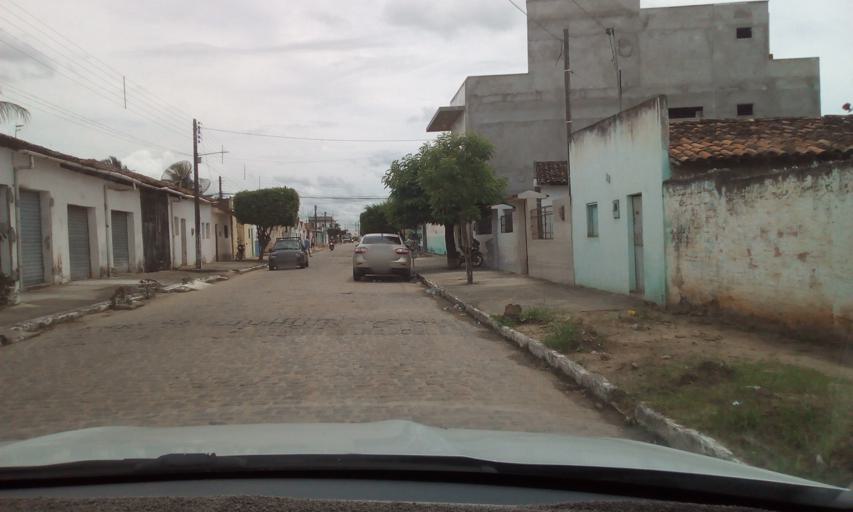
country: BR
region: Paraiba
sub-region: Mari
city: Mari
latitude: -7.0570
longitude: -35.3162
